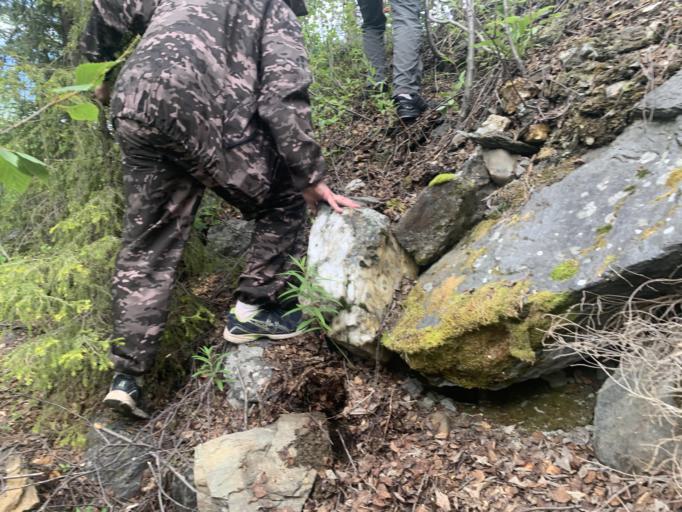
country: RU
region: Murmansk
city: Monchegorsk
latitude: 67.8734
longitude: 33.0848
